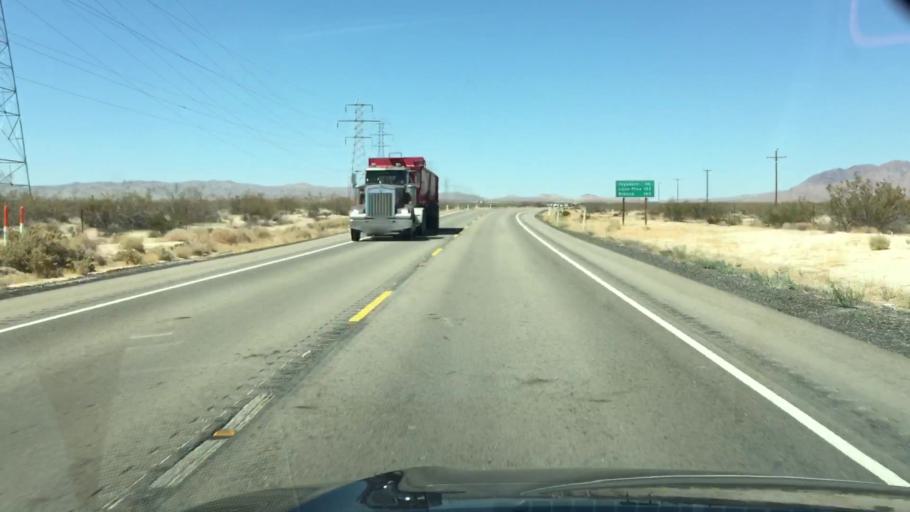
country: US
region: California
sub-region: Kern County
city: Boron
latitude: 35.2334
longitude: -117.6088
